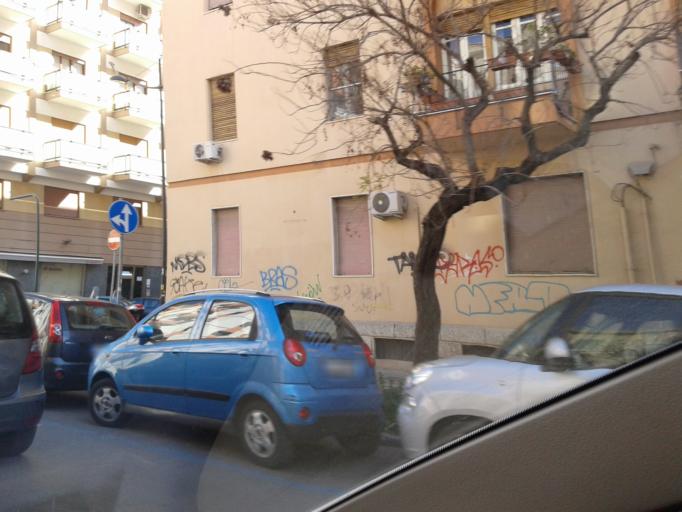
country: IT
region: Sicily
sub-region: Palermo
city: Palermo
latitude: 38.1335
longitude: 13.3462
